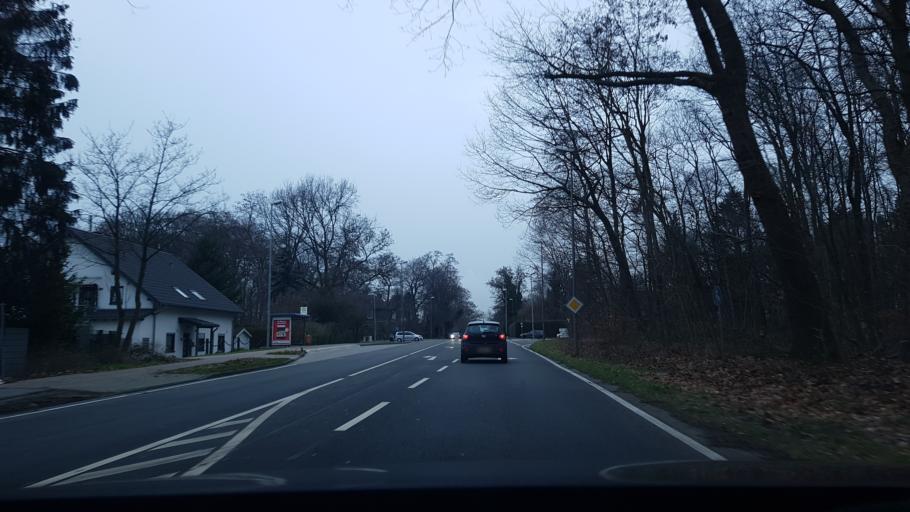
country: DE
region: North Rhine-Westphalia
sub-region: Regierungsbezirk Dusseldorf
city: Moers
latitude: 51.4303
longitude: 6.6488
